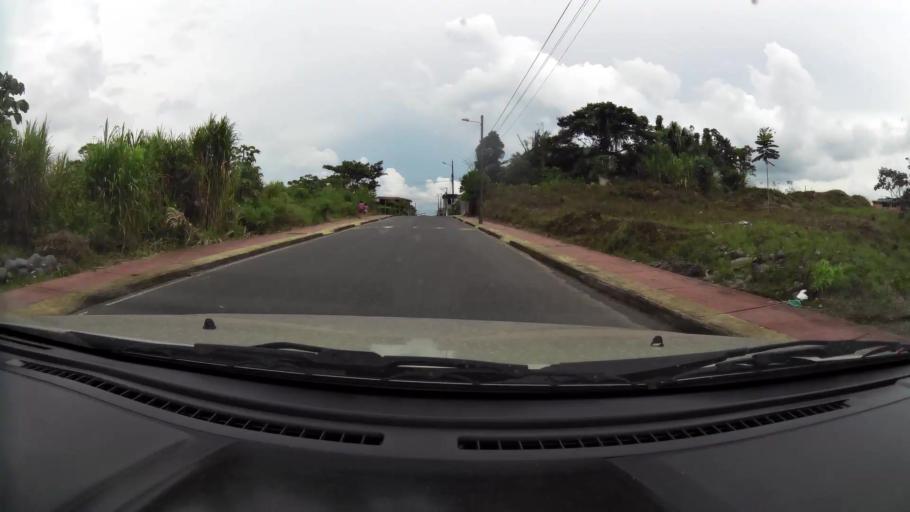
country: EC
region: Pastaza
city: Puyo
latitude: -1.4906
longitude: -78.0028
